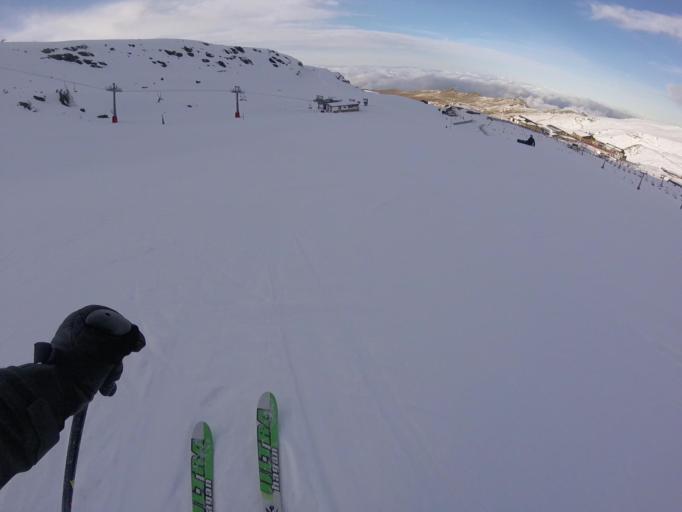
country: ES
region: Andalusia
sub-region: Provincia de Granada
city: Guejar-Sierra
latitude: 37.0672
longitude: -3.3902
